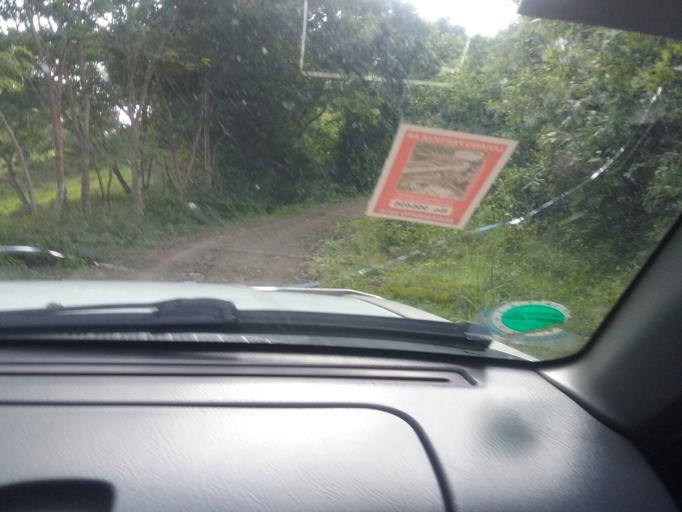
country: NI
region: Matagalpa
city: Matagalpa
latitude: 12.8708
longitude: -85.9362
